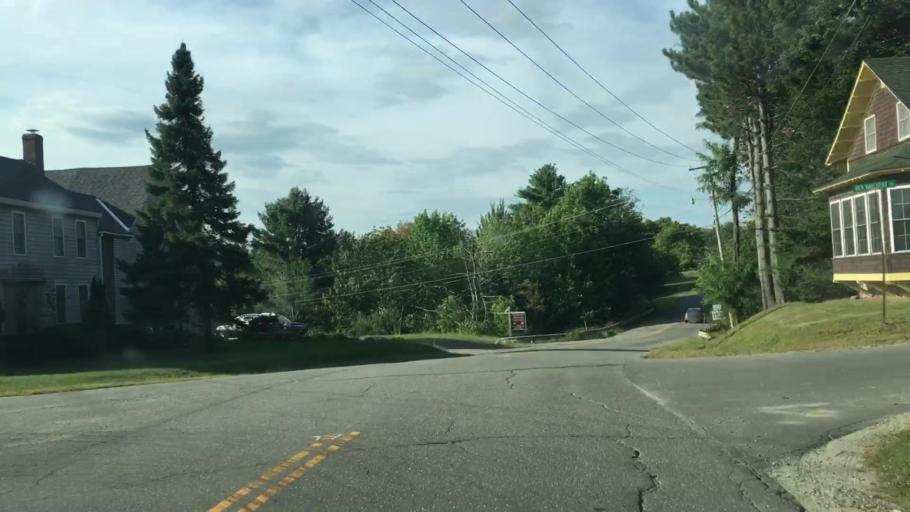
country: US
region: Maine
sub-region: Penobscot County
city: Enfield
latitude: 45.2465
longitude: -68.5659
